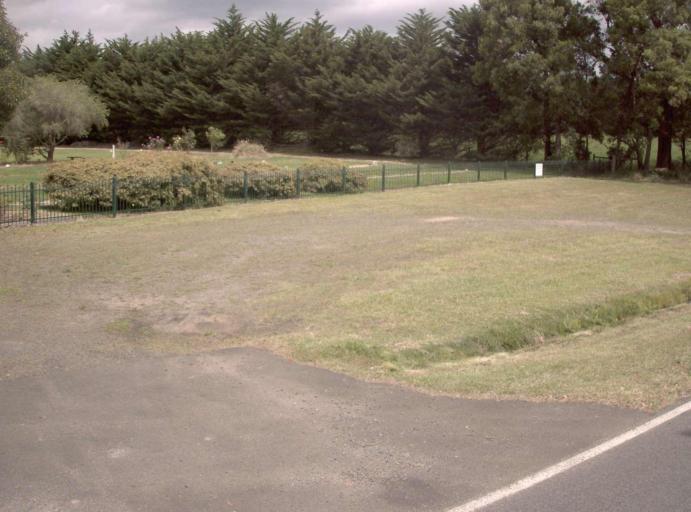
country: AU
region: Victoria
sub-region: Latrobe
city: Moe
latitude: -38.0692
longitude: 146.1757
